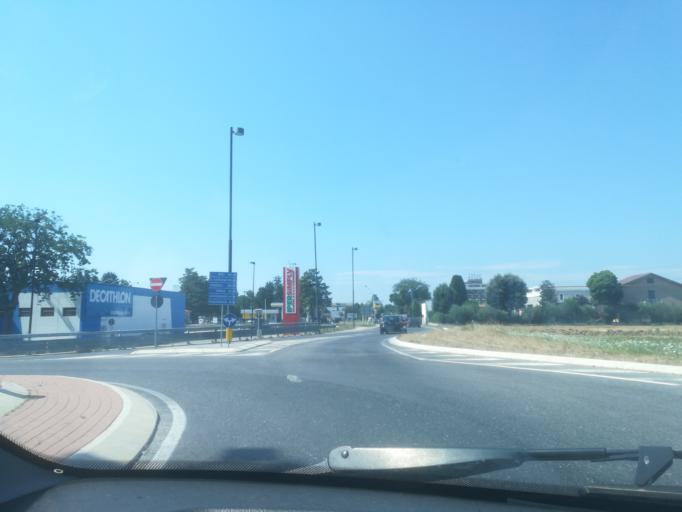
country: IT
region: The Marches
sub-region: Provincia di Macerata
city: Villa Potenza
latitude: 43.3393
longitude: 13.4367
